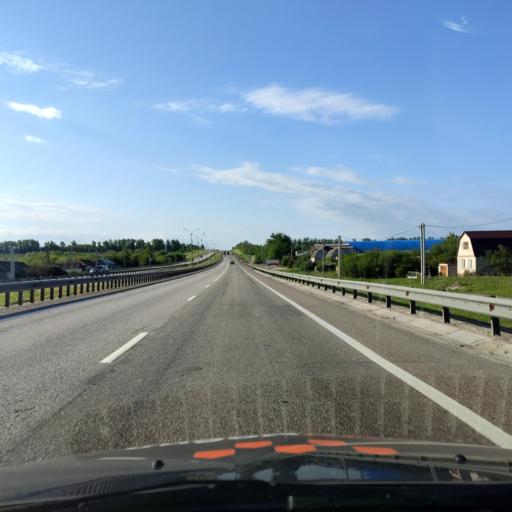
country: RU
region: Voronezj
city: Ramon'
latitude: 52.0382
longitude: 39.1991
